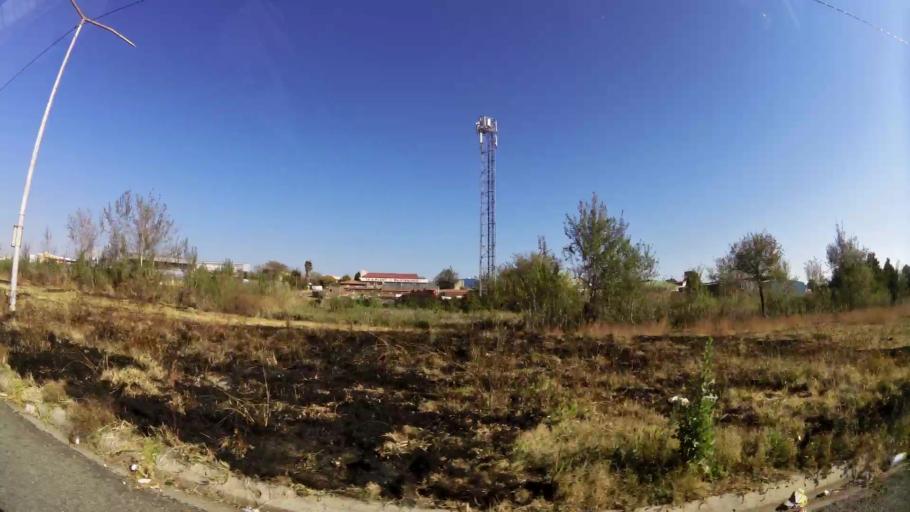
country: ZA
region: Gauteng
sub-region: City of Johannesburg Metropolitan Municipality
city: Modderfontein
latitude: -26.0643
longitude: 28.1973
